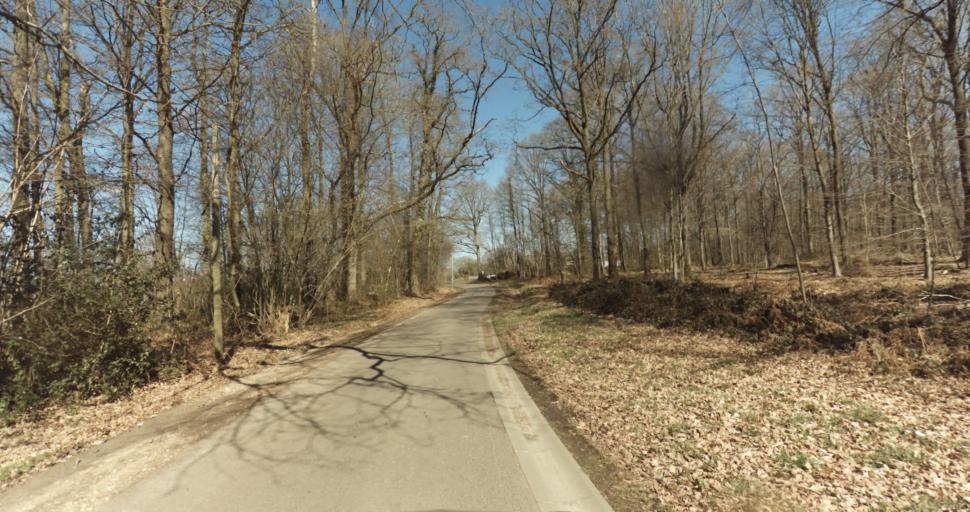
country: FR
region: Lower Normandy
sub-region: Departement du Calvados
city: Livarot
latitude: 48.9729
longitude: 0.0948
